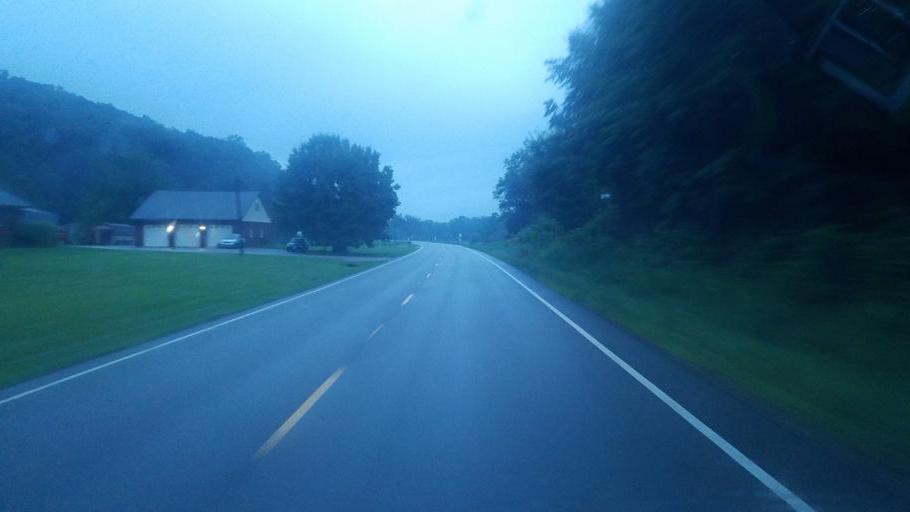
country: US
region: Ohio
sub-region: Knox County
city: Oak Hill
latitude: 40.3371
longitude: -82.0825
